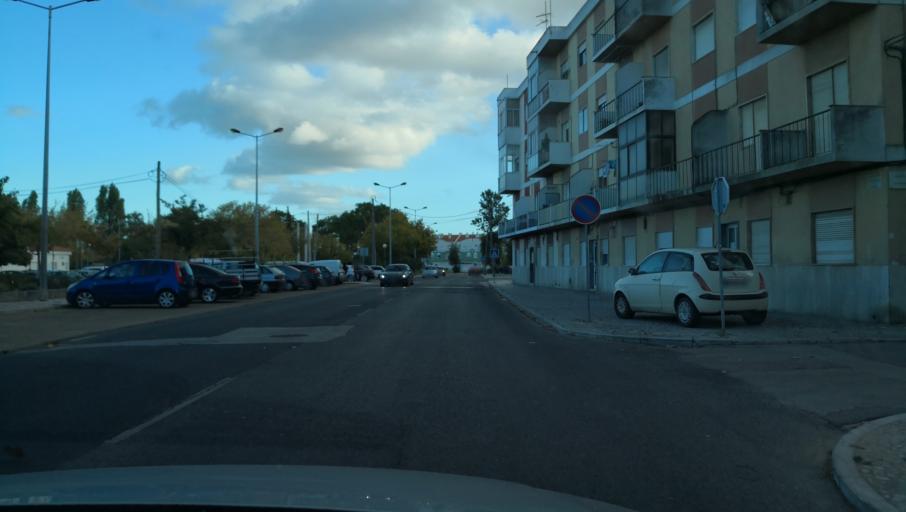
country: PT
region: Setubal
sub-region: Moita
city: Alhos Vedros
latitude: 38.6633
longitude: -9.0438
